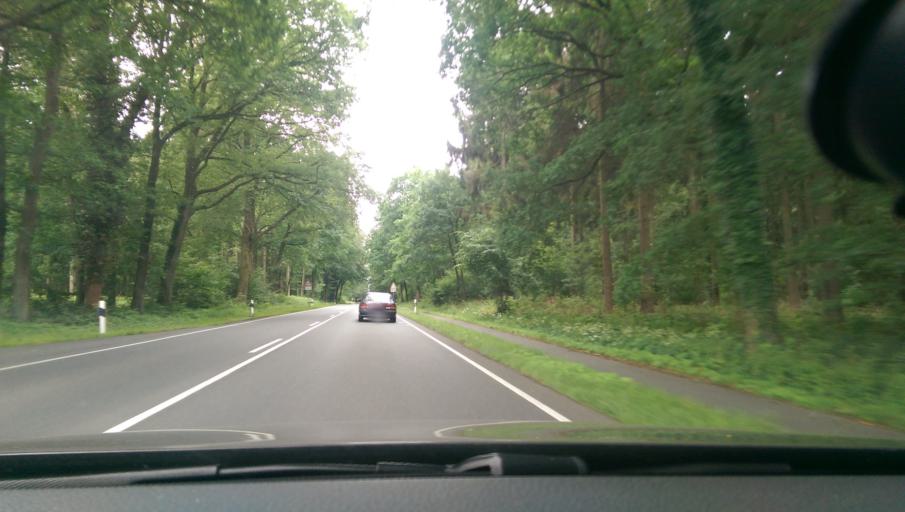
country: DE
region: Lower Saxony
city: Kirchlinteln
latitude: 53.0022
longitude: 9.2700
